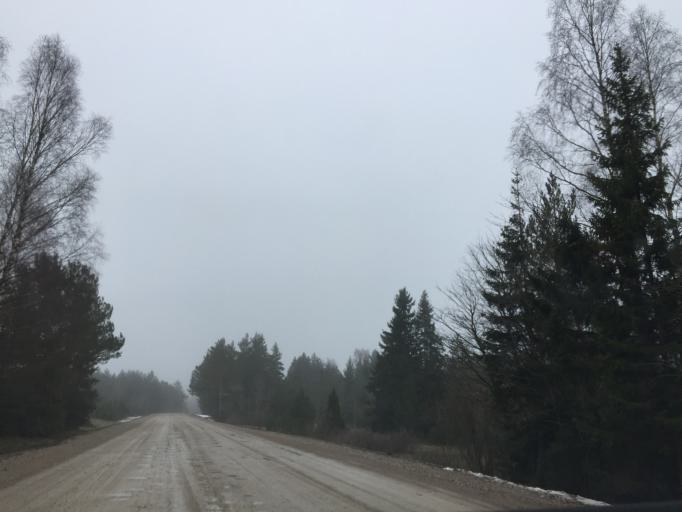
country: EE
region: Saare
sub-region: Kuressaare linn
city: Kuressaare
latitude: 58.4787
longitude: 22.0008
